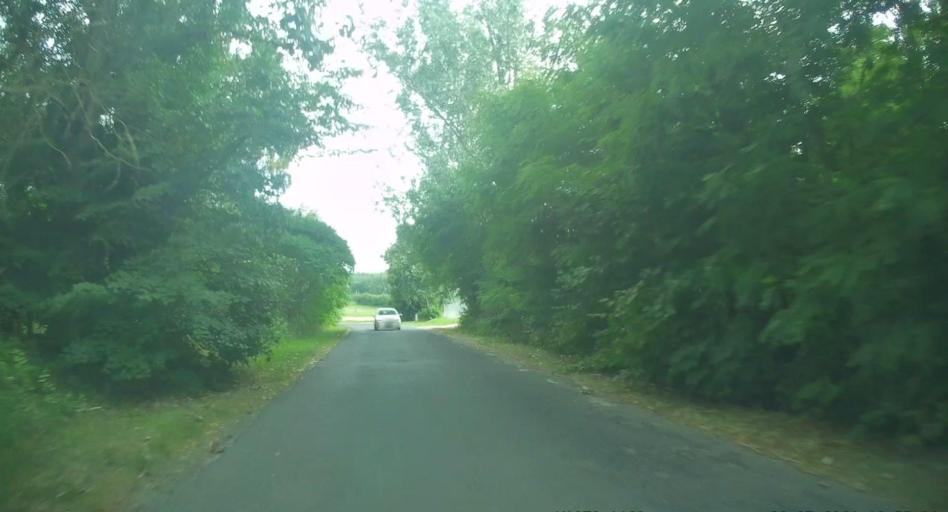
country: PL
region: Lodz Voivodeship
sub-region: Powiat rawski
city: Rawa Mazowiecka
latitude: 51.7721
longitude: 20.1817
